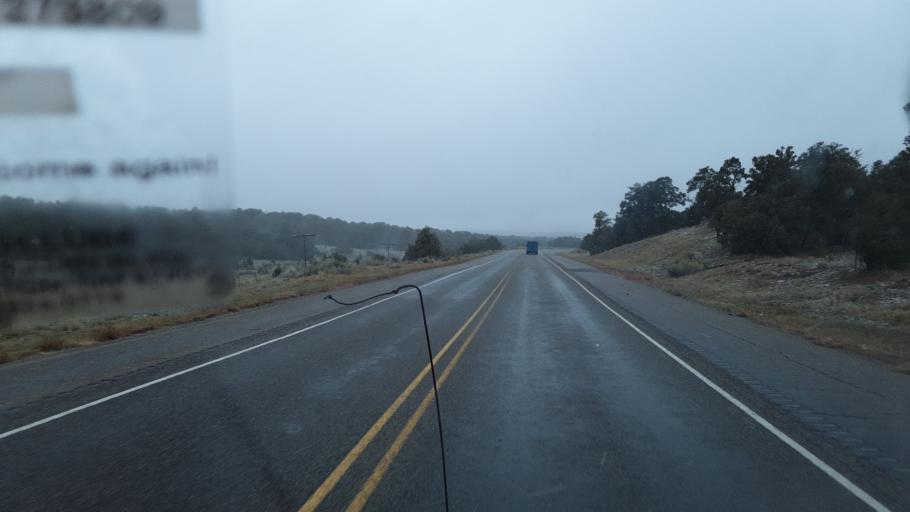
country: US
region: New Mexico
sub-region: Rio Arriba County
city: Tierra Amarilla
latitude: 36.4693
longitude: -106.4836
